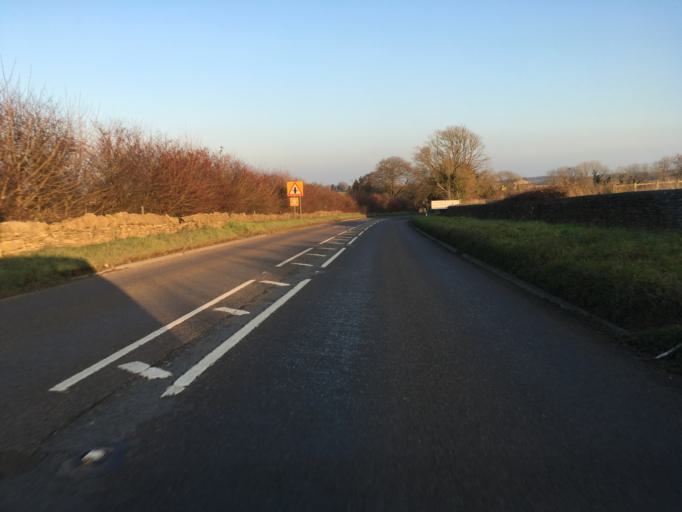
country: GB
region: England
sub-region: Wiltshire
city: Colerne
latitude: 51.4668
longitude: -2.2808
